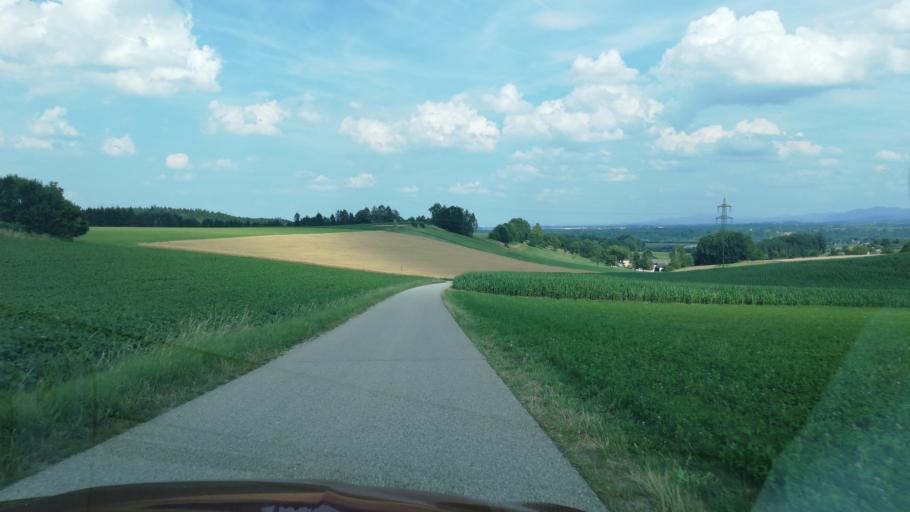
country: AT
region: Upper Austria
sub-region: Politischer Bezirk Vocklabruck
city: Puhret
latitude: 48.0365
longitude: 13.7157
